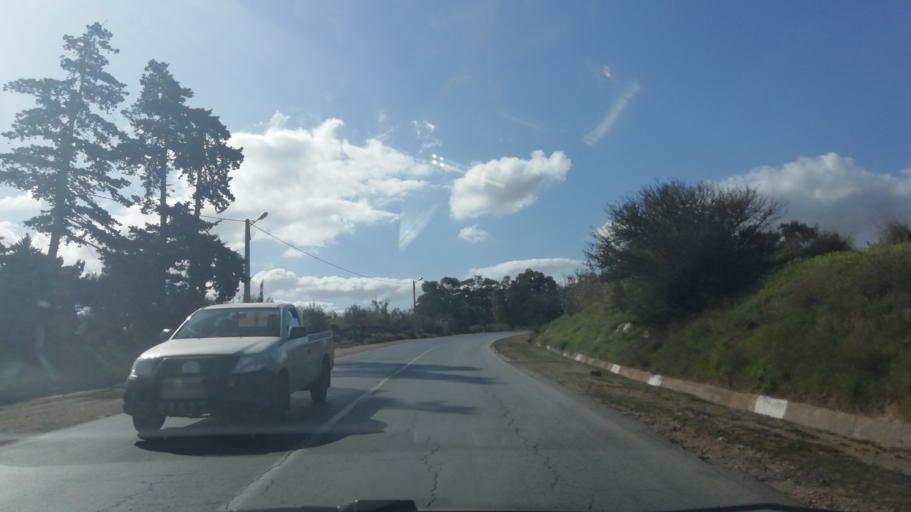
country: DZ
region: Relizane
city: Mazouna
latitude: 36.2975
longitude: 0.6578
